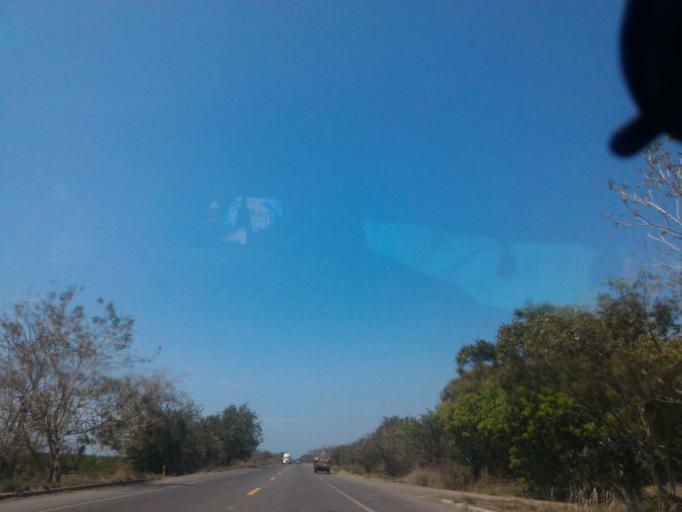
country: MX
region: Michoacan
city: Coahuayana Viejo
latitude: 18.7811
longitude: -103.7657
